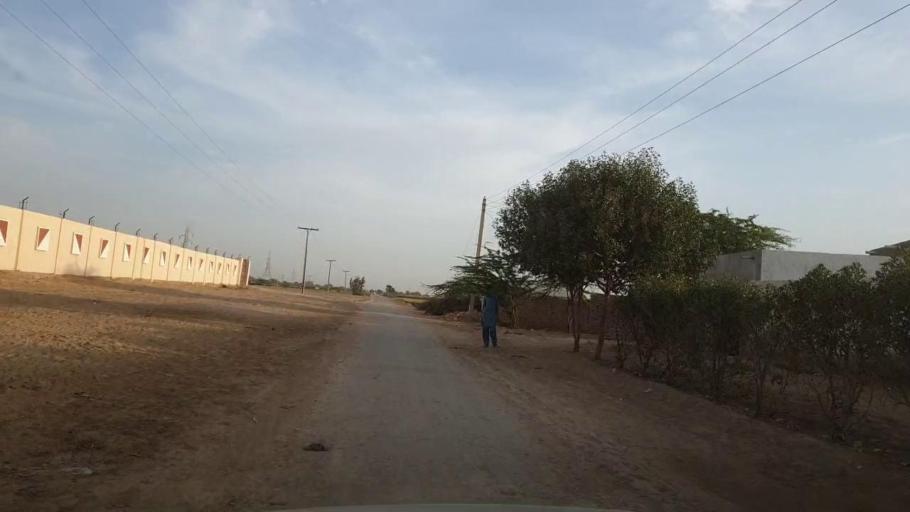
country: PK
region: Sindh
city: Kunri
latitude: 25.1745
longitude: 69.5422
